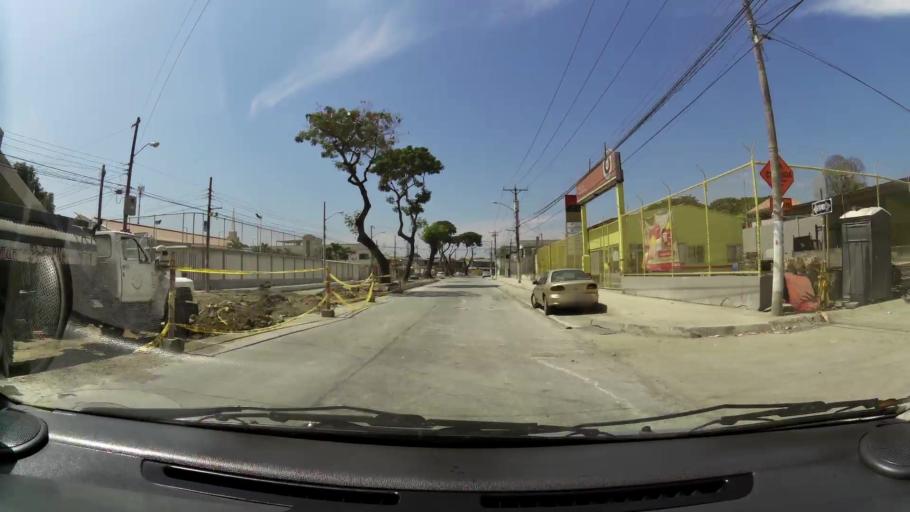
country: EC
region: Guayas
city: Eloy Alfaro
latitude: -2.1134
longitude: -79.9039
